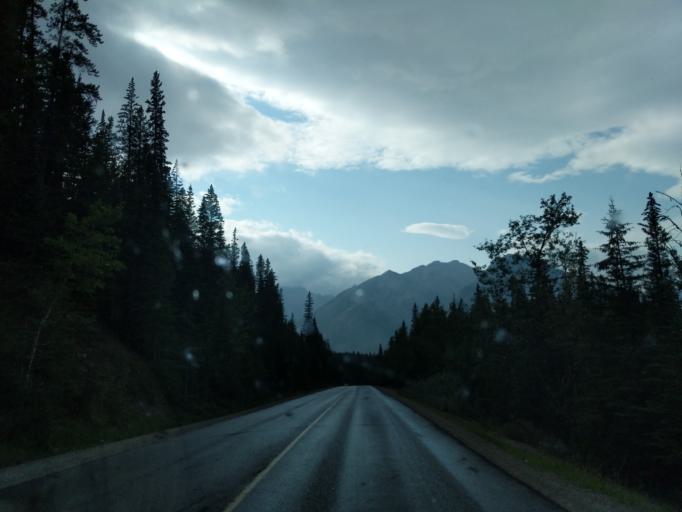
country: CA
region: Alberta
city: Banff
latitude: 51.1625
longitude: -115.5732
